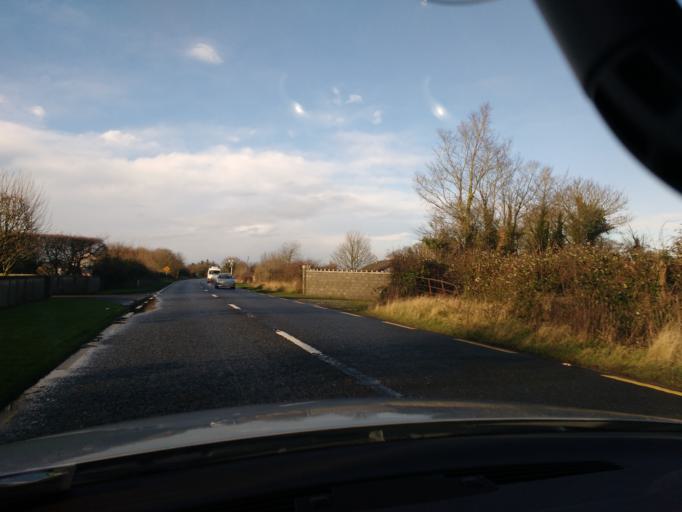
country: IE
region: Munster
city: Thurles
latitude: 52.6387
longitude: -7.7830
